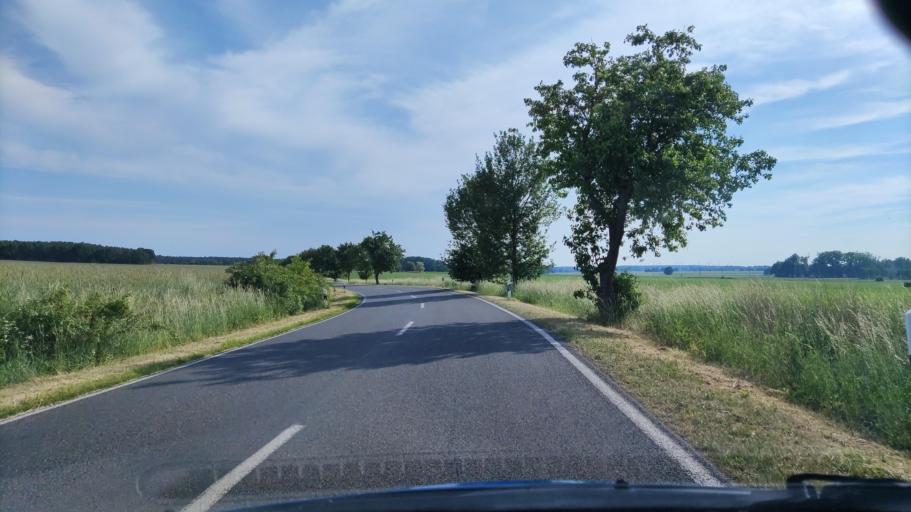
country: DE
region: Saxony-Anhalt
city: Klotze
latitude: 52.6586
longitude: 11.1999
